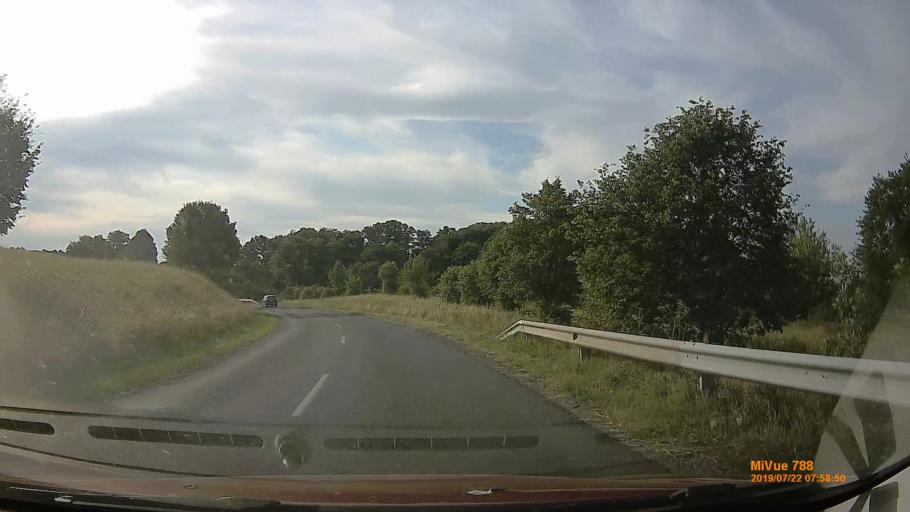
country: HU
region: Veszprem
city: Urkut
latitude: 47.0062
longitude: 17.6011
